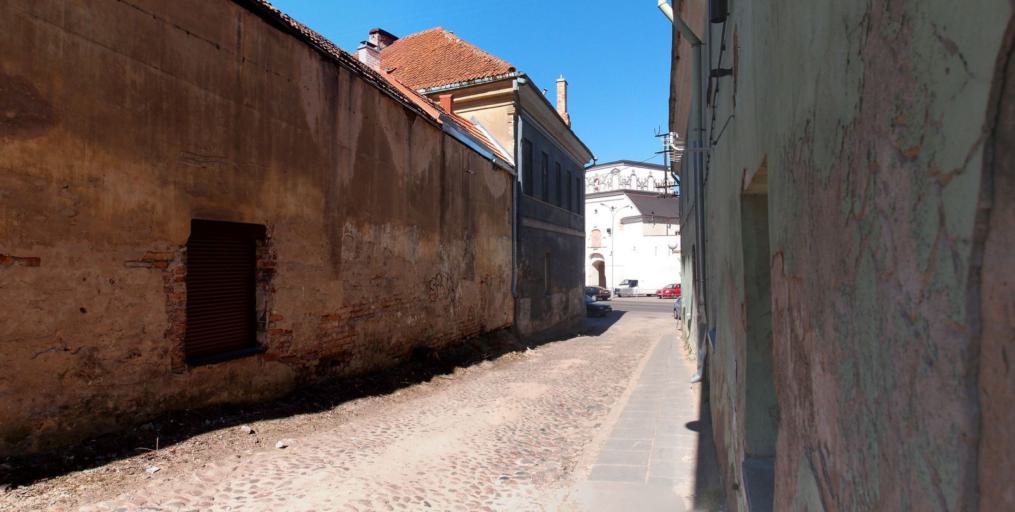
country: LT
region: Vilnius County
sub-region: Vilnius
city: Vilnius
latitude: 54.6738
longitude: 25.2905
